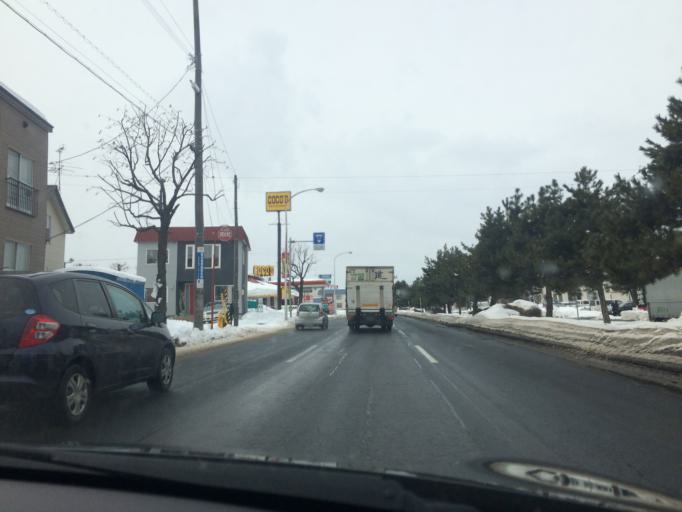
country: JP
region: Hokkaido
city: Sapporo
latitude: 43.0814
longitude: 141.3876
